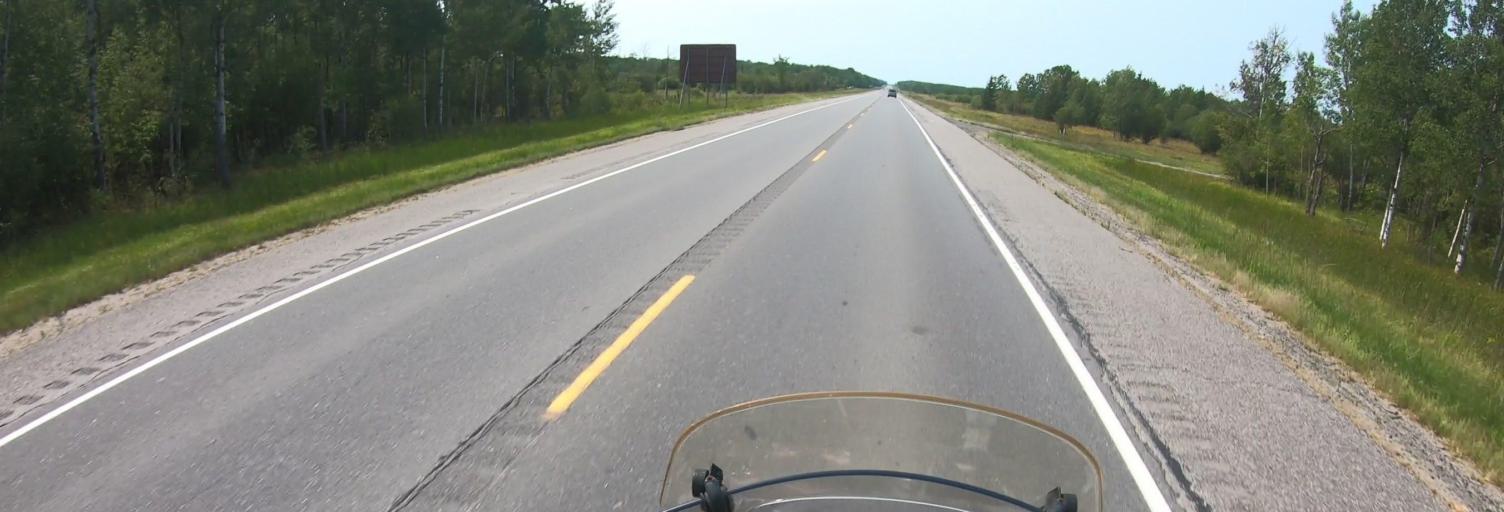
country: US
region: Minnesota
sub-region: Koochiching County
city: International Falls
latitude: 48.5522
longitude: -93.4465
